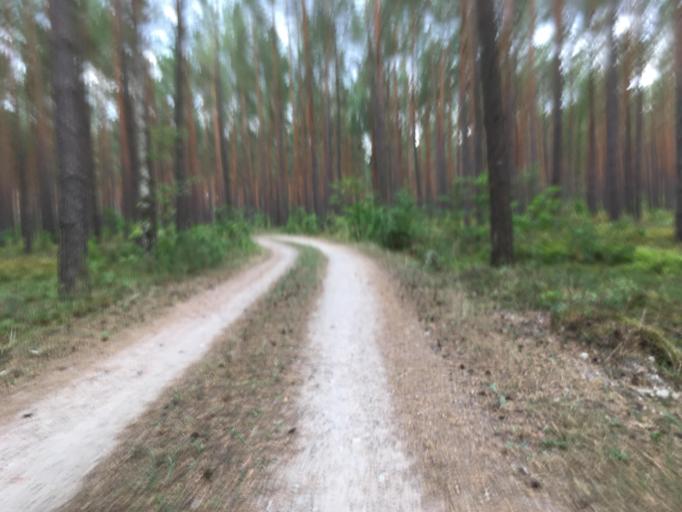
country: DE
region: Brandenburg
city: Furstenberg
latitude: 53.1252
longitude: 13.2412
